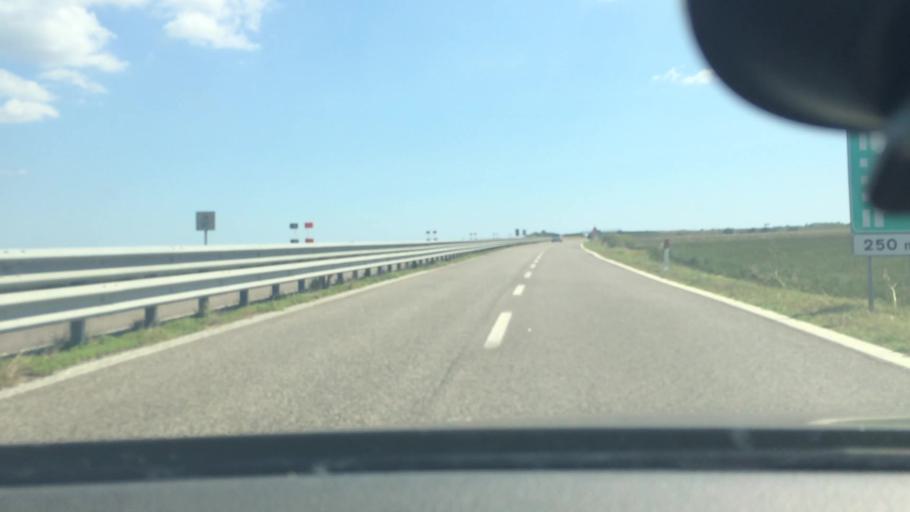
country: IT
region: Emilia-Romagna
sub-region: Provincia di Ferrara
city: Ostellato
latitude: 44.7560
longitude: 11.9715
